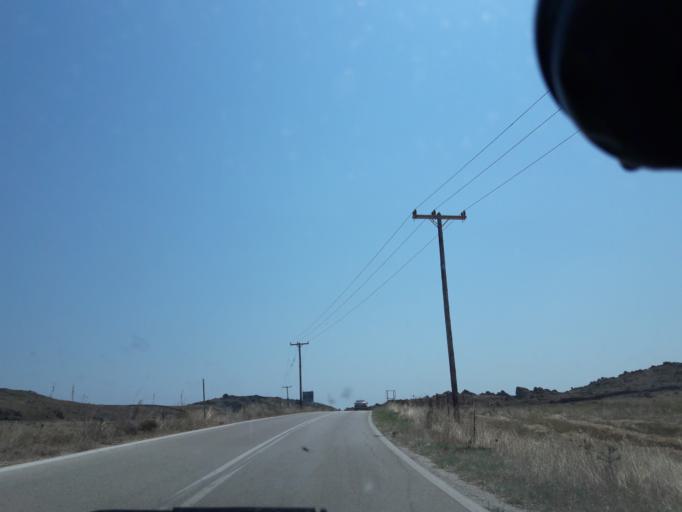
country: GR
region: North Aegean
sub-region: Nomos Lesvou
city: Myrina
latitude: 39.8582
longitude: 25.1425
